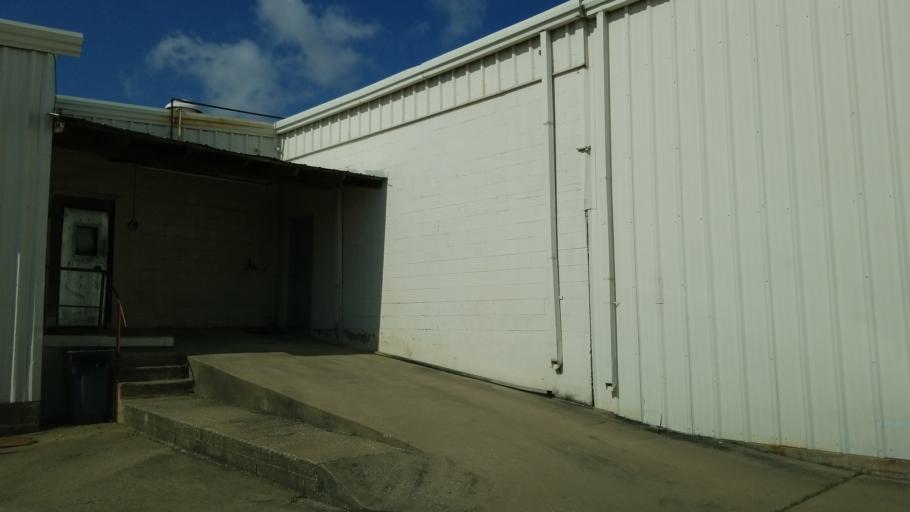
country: US
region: Texas
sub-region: Dallas County
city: Farmers Branch
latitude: 32.8871
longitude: -96.8950
